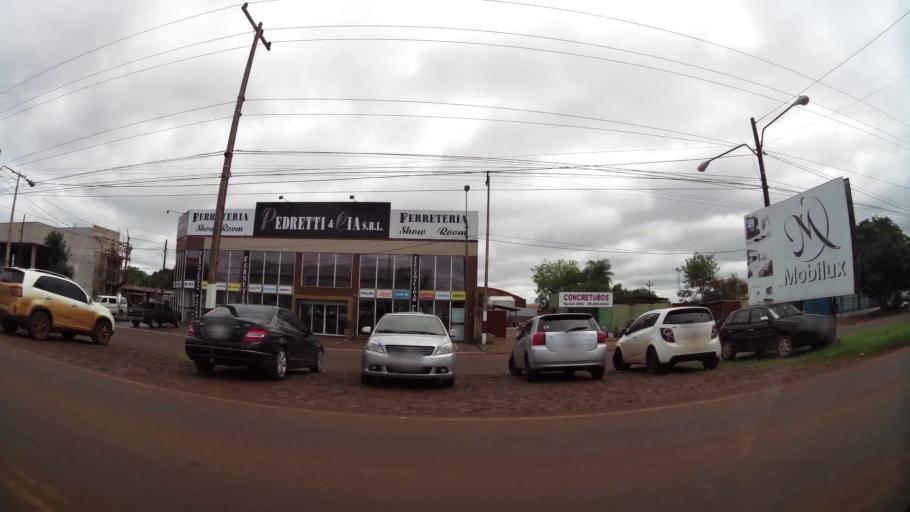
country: PY
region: Alto Parana
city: Ciudad del Este
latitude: -25.3894
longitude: -54.6382
